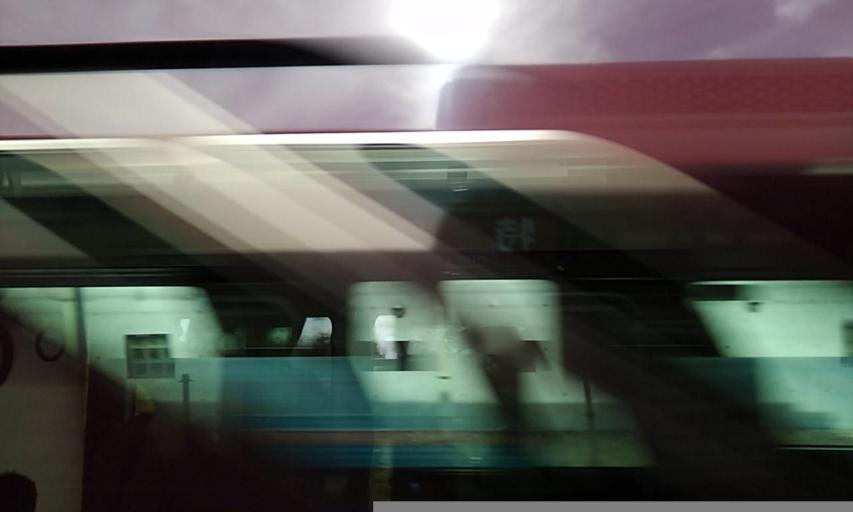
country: JP
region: Hyogo
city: Ashiya
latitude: 34.7296
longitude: 135.2810
